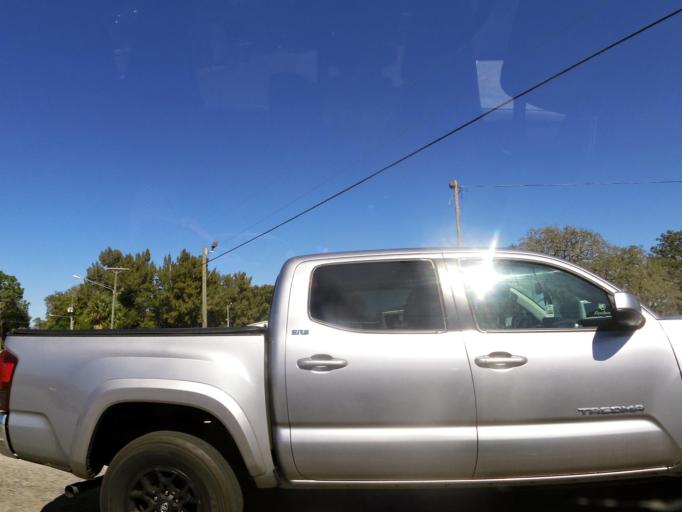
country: US
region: Florida
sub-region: Orange County
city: Lockhart
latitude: 28.6174
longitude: -81.4391
